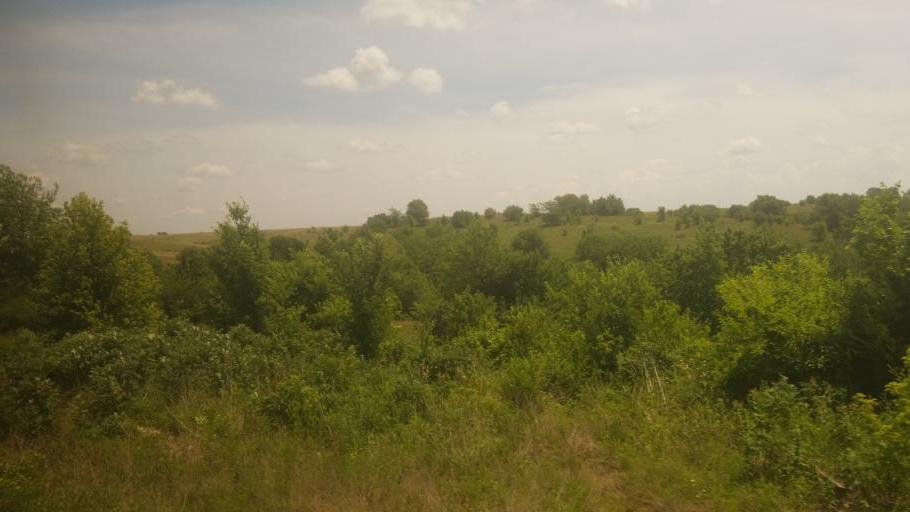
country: US
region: Missouri
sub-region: Linn County
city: Marceline
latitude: 39.8491
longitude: -92.8131
